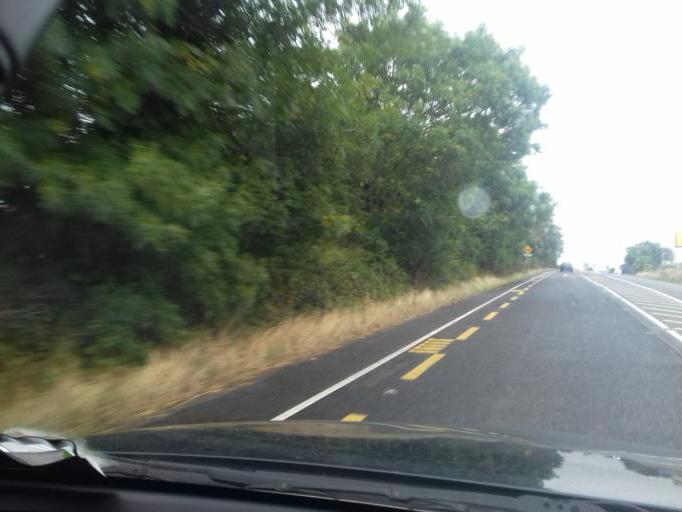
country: IE
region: Leinster
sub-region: County Carlow
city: Bagenalstown
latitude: 52.7578
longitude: -6.9572
